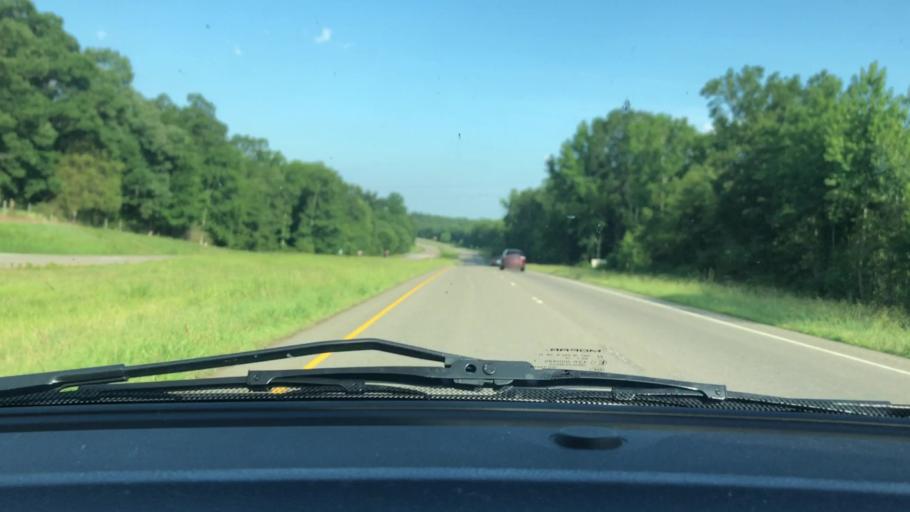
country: US
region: North Carolina
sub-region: Chatham County
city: Farmville
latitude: 35.6146
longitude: -79.3471
